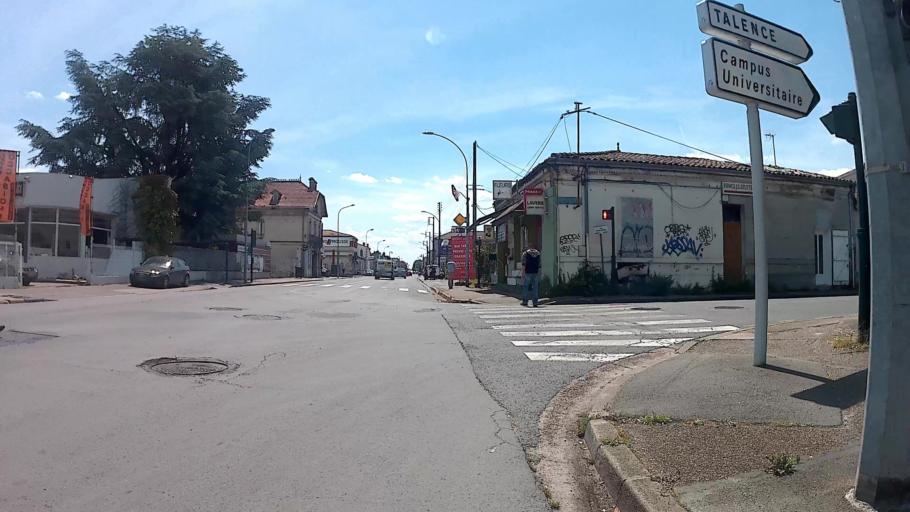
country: FR
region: Aquitaine
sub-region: Departement de la Gironde
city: Talence
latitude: 44.8138
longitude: -0.5781
